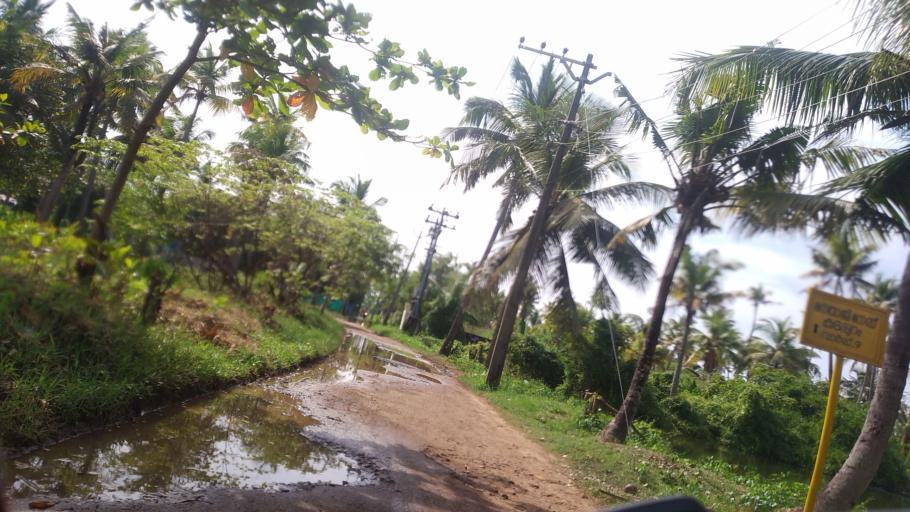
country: IN
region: Kerala
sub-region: Ernakulam
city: Elur
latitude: 10.0828
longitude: 76.2013
